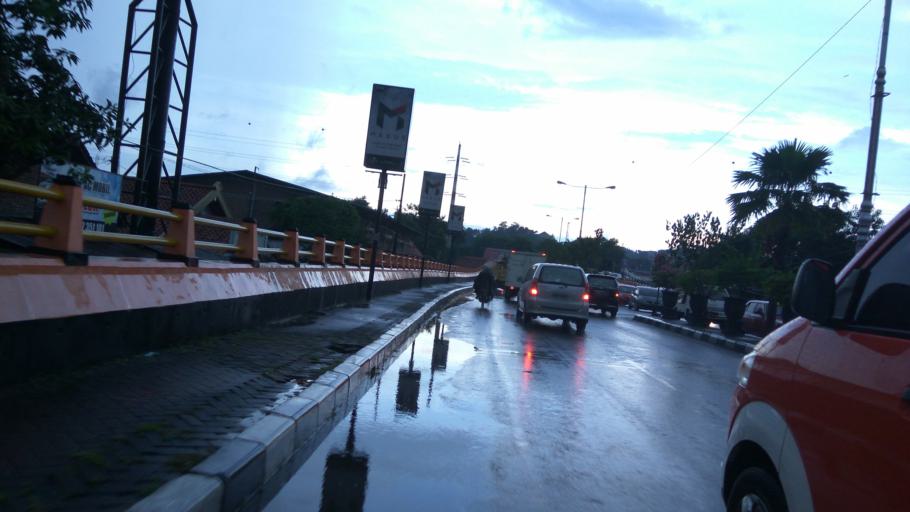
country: ID
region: Central Java
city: Semarang
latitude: -6.9949
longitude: 110.4003
